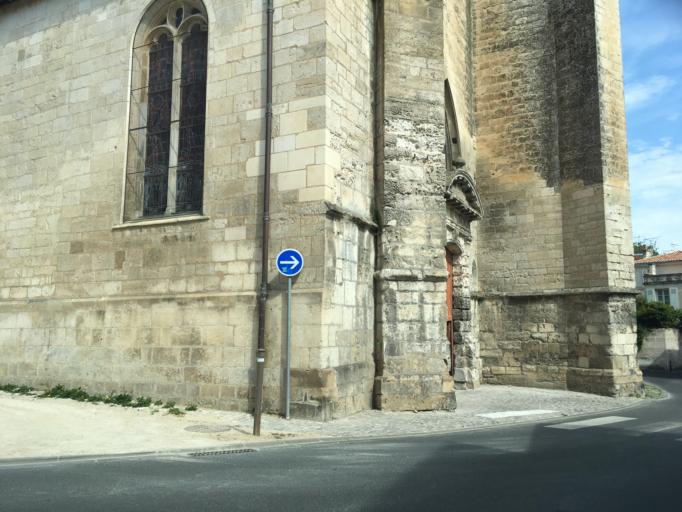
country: FR
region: Poitou-Charentes
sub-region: Departement des Deux-Sevres
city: Niort
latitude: 46.3227
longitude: -0.4656
